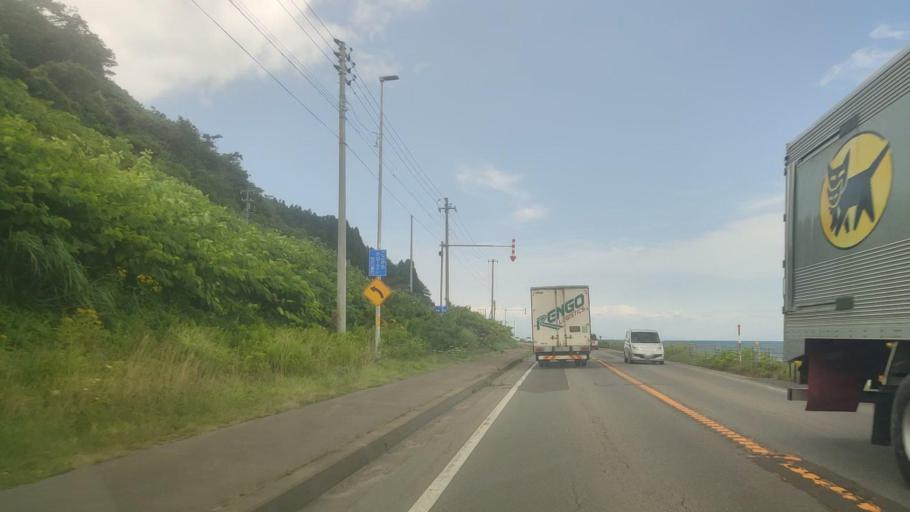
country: JP
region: Hokkaido
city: Nanae
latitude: 42.1452
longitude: 140.5000
